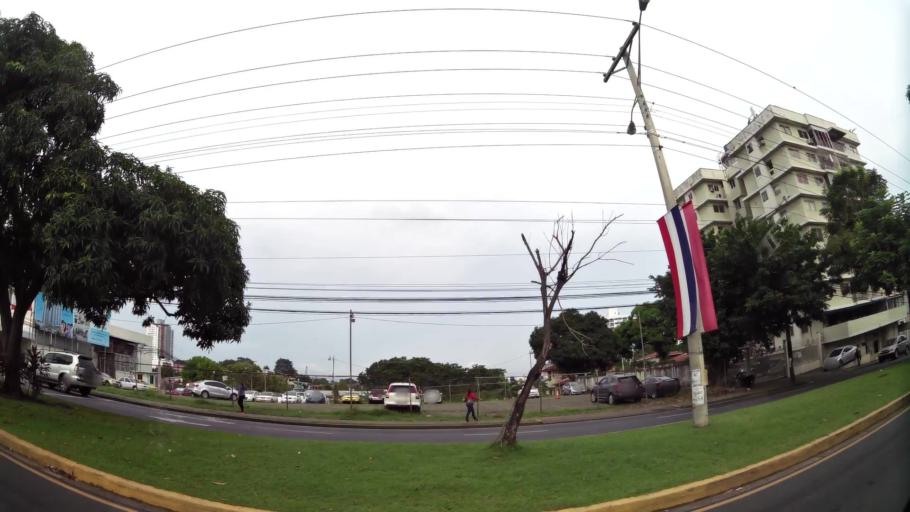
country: PA
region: Panama
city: Panama
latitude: 9.0099
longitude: -79.5086
